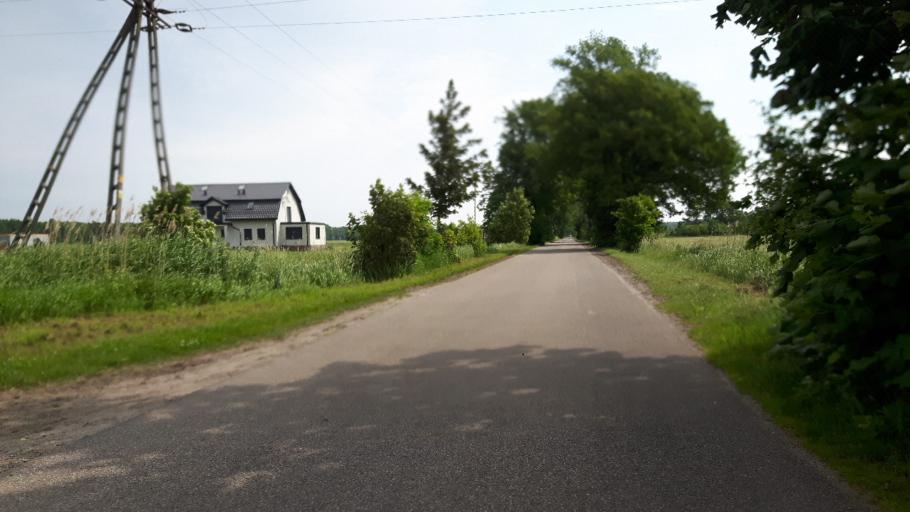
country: PL
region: Pomeranian Voivodeship
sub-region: Powiat leborski
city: Leba
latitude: 54.7512
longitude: 17.5925
